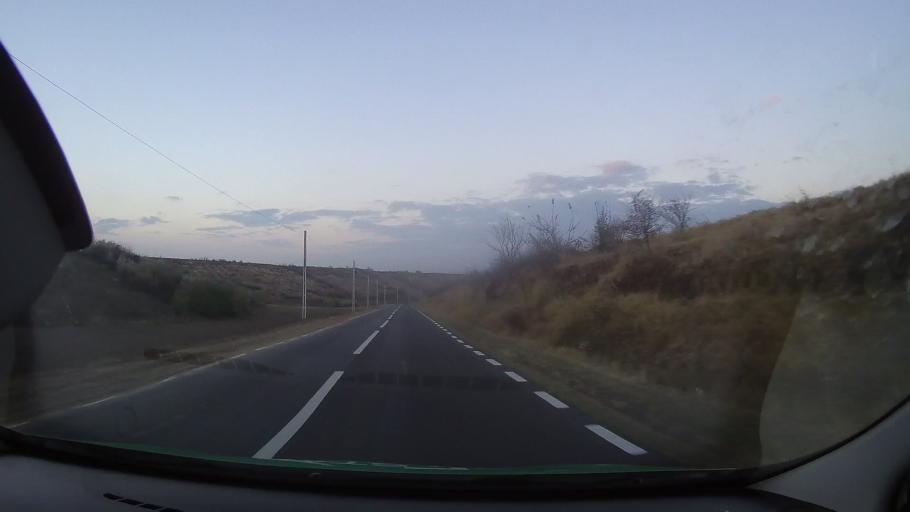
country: RO
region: Constanta
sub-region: Comuna Oltina
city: Oltina
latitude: 44.1362
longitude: 27.6665
